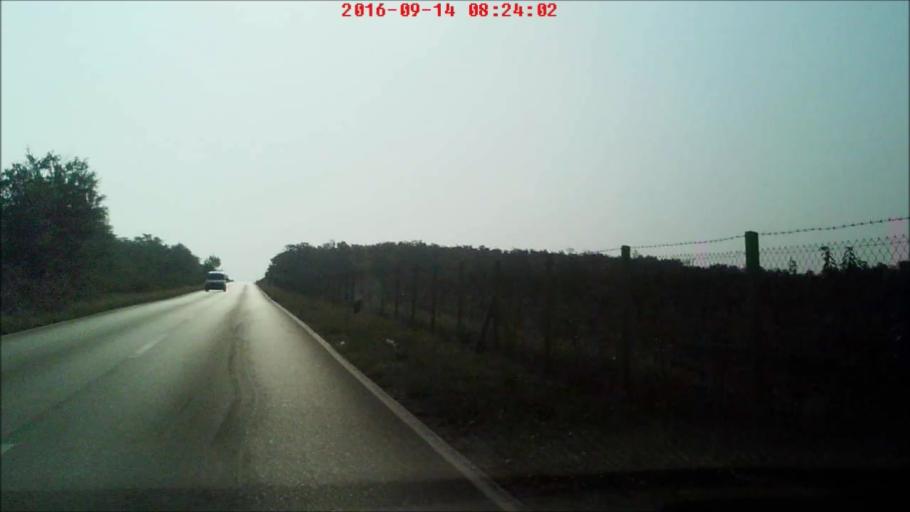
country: HR
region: Zadarska
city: Vrsi
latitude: 44.2083
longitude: 15.2384
